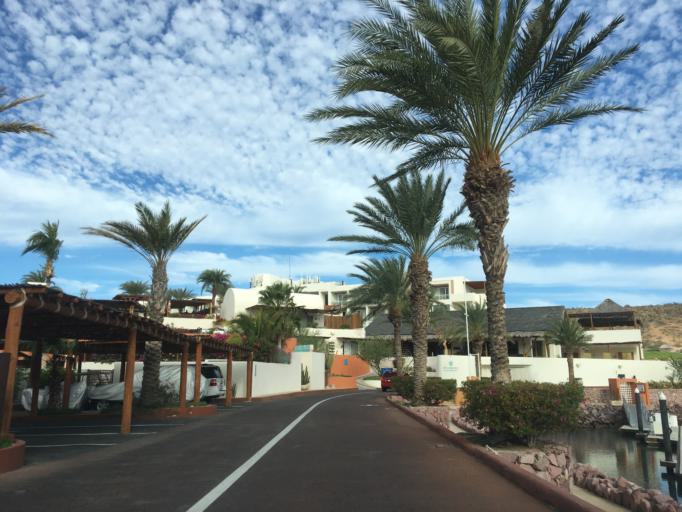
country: MX
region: Baja California Sur
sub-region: La Paz
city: La Paz
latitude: 24.2170
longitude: -110.3005
